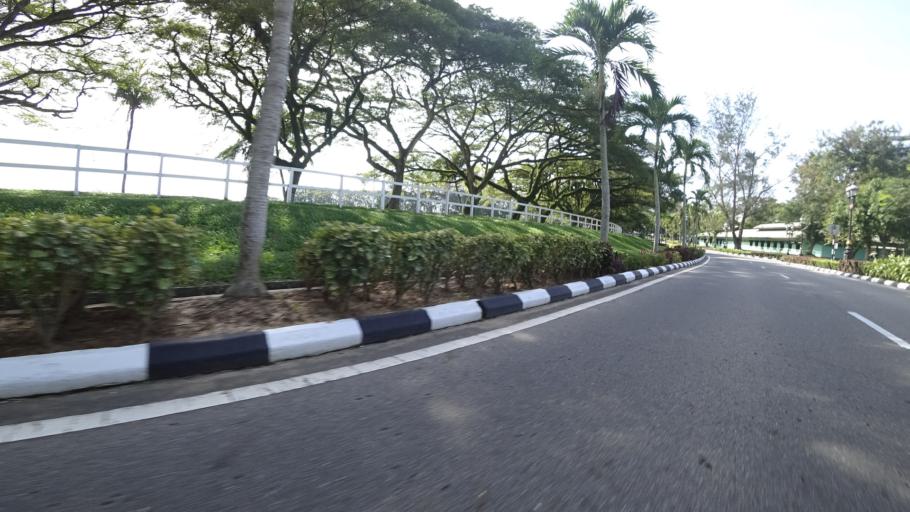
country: BN
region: Brunei and Muara
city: Bandar Seri Begawan
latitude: 4.9474
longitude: 114.8331
